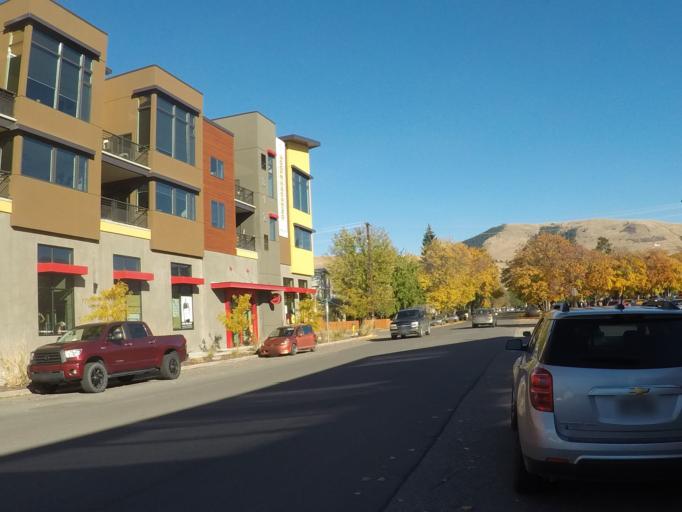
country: US
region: Montana
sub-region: Missoula County
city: Missoula
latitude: 46.8780
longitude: -114.0026
